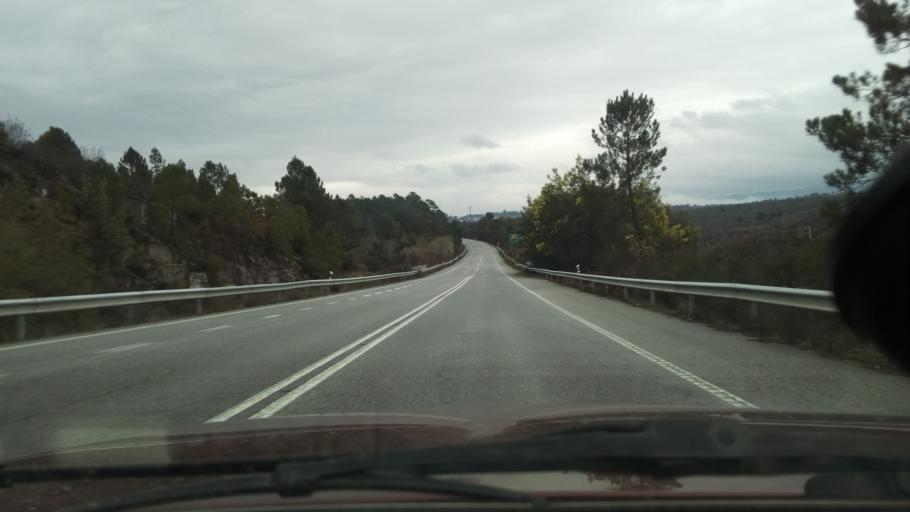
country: PT
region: Guarda
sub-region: Fornos de Algodres
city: Fornos de Algodres
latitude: 40.6035
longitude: -7.5463
